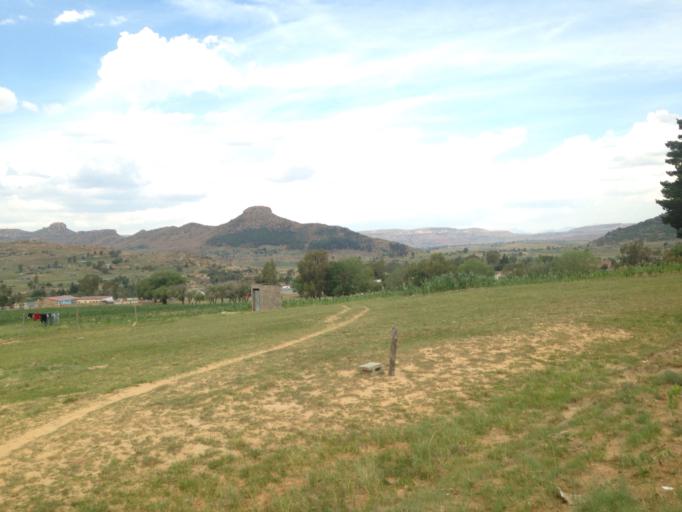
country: LS
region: Mafeteng
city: Mafeteng
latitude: -29.6922
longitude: 27.4320
